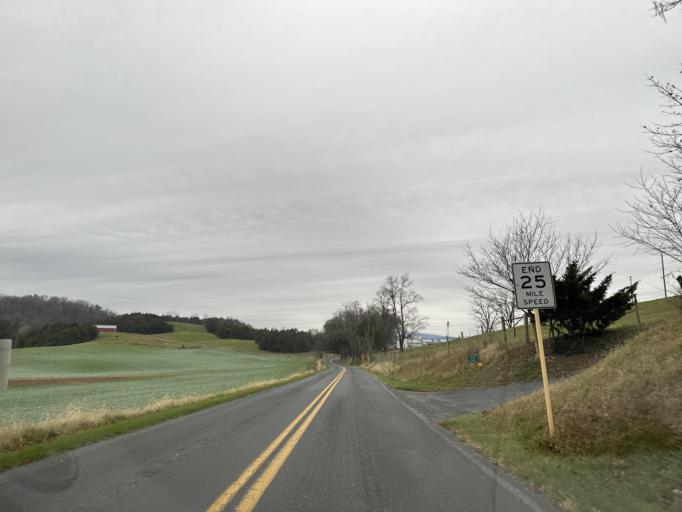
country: US
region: Virginia
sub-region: Rockingham County
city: Bridgewater
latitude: 38.3468
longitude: -79.0876
